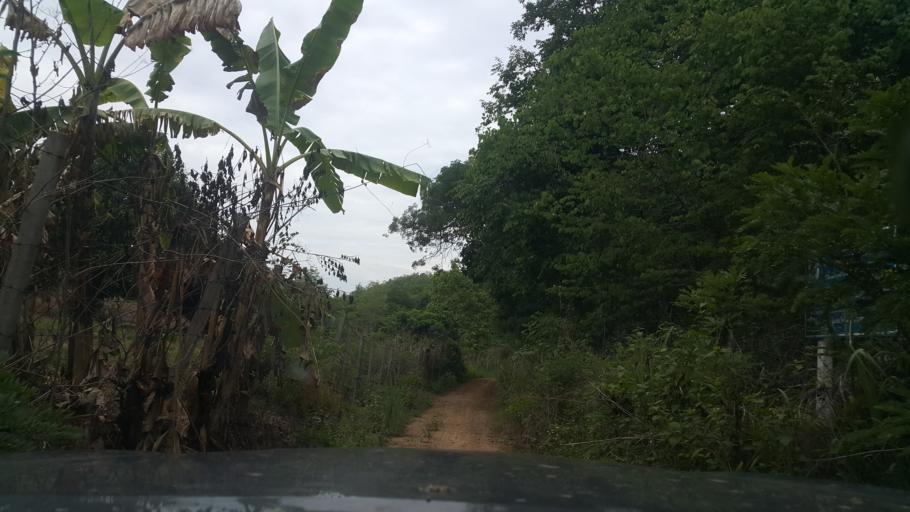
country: TH
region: Chiang Mai
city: Hang Dong
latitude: 18.6878
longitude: 98.8440
